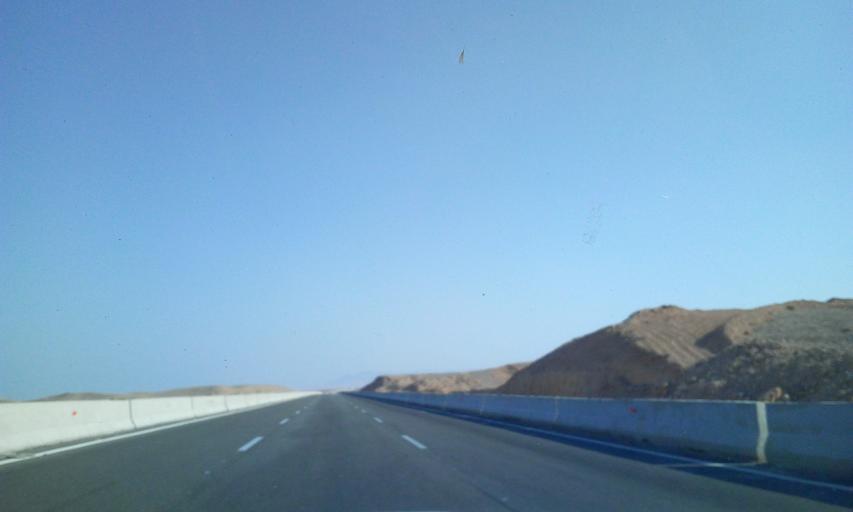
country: EG
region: As Suways
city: Ain Sukhna
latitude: 29.2286
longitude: 32.4873
